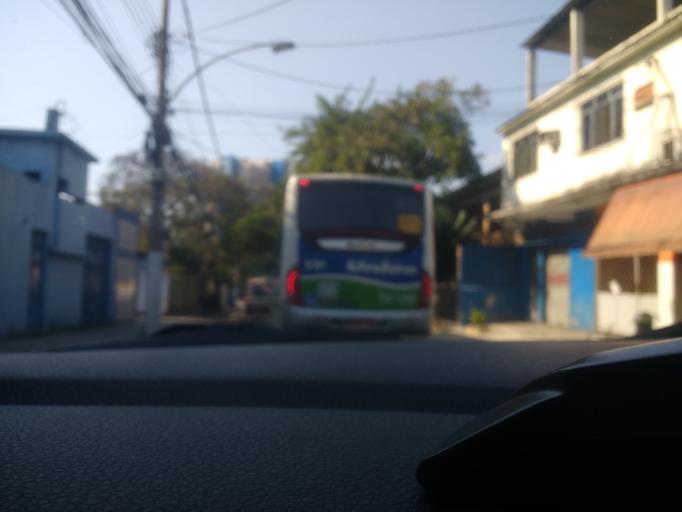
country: BR
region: Rio de Janeiro
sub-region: Duque De Caxias
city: Duque de Caxias
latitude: -22.7945
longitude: -43.2985
